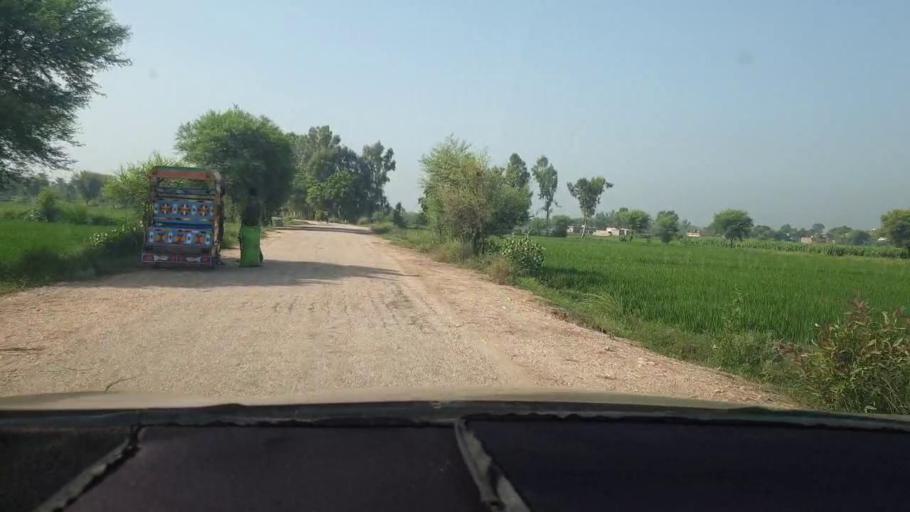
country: PK
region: Sindh
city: Kambar
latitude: 27.6129
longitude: 68.0909
